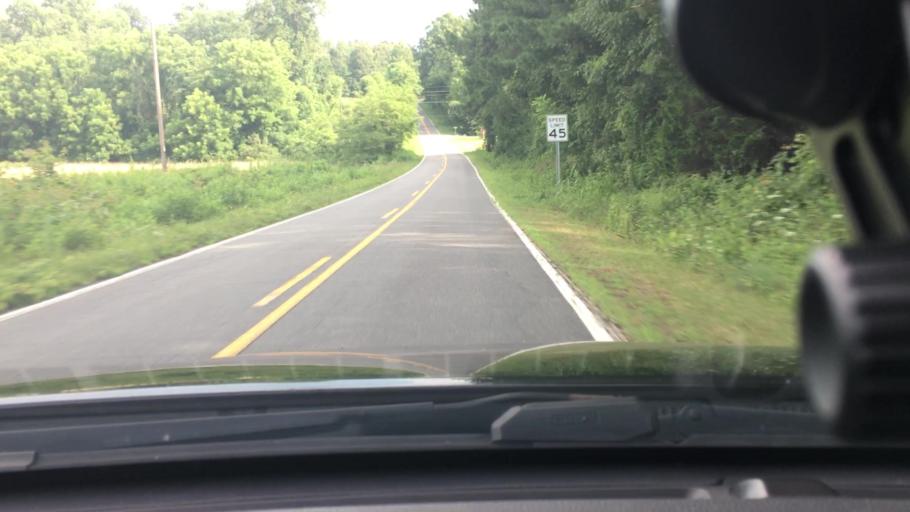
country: US
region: North Carolina
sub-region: Rutherford County
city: Rutherfordton
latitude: 35.3955
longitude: -81.9715
